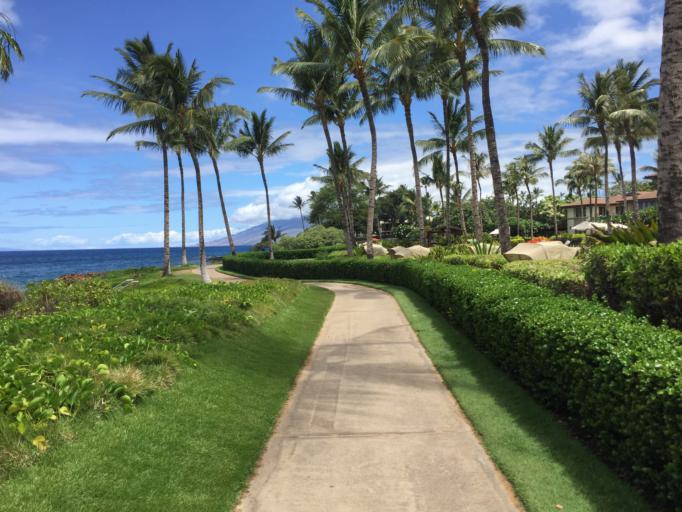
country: US
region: Hawaii
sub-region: Maui County
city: Kihei
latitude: 20.6843
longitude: -156.4430
